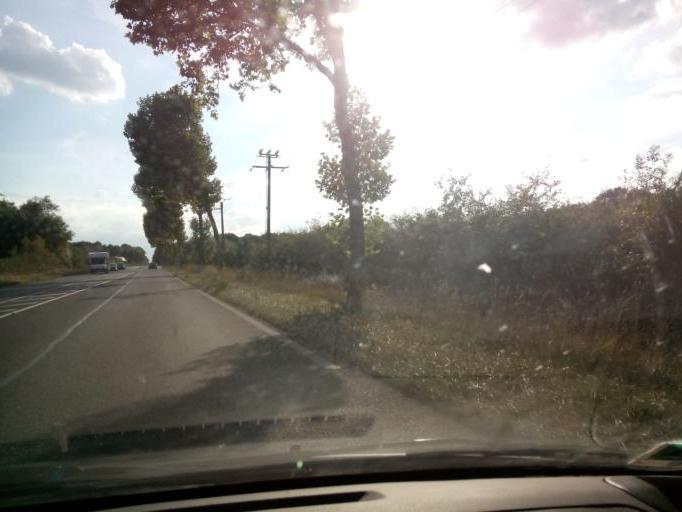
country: FR
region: Centre
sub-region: Departement d'Indre-et-Loire
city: Sache
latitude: 47.2953
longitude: 0.5398
